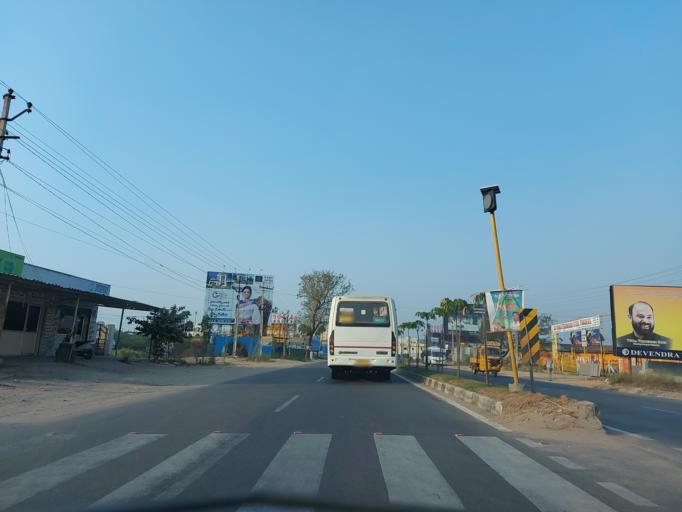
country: IN
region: Telangana
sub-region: Rangareddi
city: Balapur
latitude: 17.2007
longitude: 78.4758
